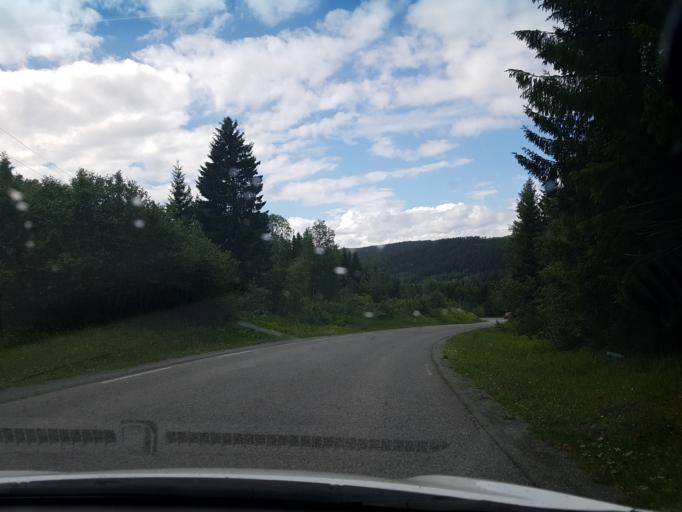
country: NO
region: Nord-Trondelag
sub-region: Stjordal
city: Stjordalshalsen
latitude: 63.6077
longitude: 10.9433
